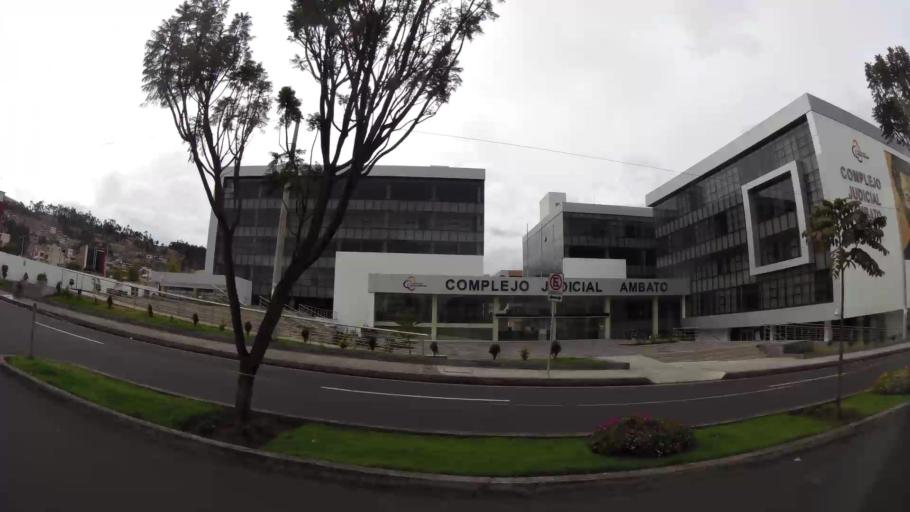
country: EC
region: Tungurahua
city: Ambato
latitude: -1.2753
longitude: -78.6382
